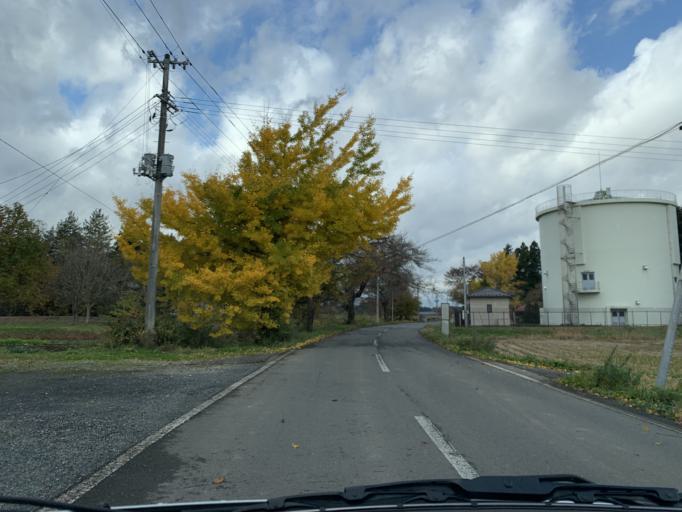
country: JP
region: Iwate
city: Mizusawa
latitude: 39.0653
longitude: 141.0816
